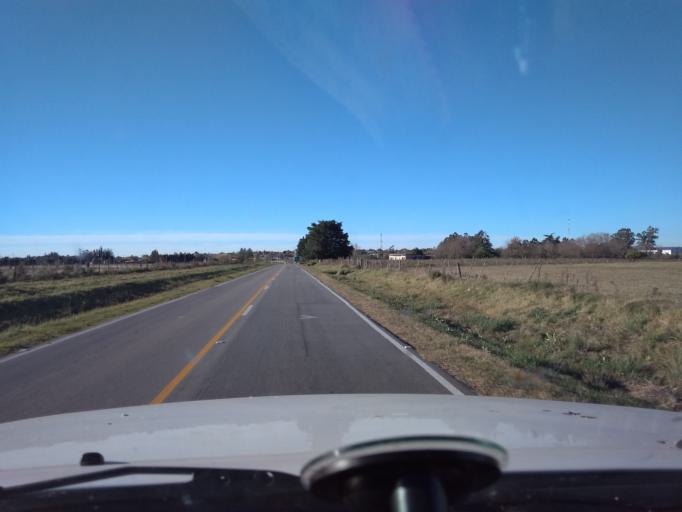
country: UY
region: Canelones
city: Santa Rosa
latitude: -34.5090
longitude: -56.0527
